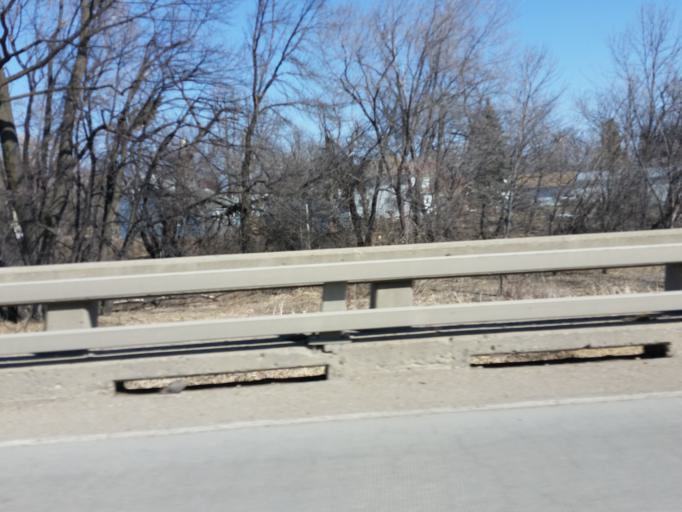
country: US
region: North Dakota
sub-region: Walsh County
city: Grafton
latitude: 48.2846
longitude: -97.3707
